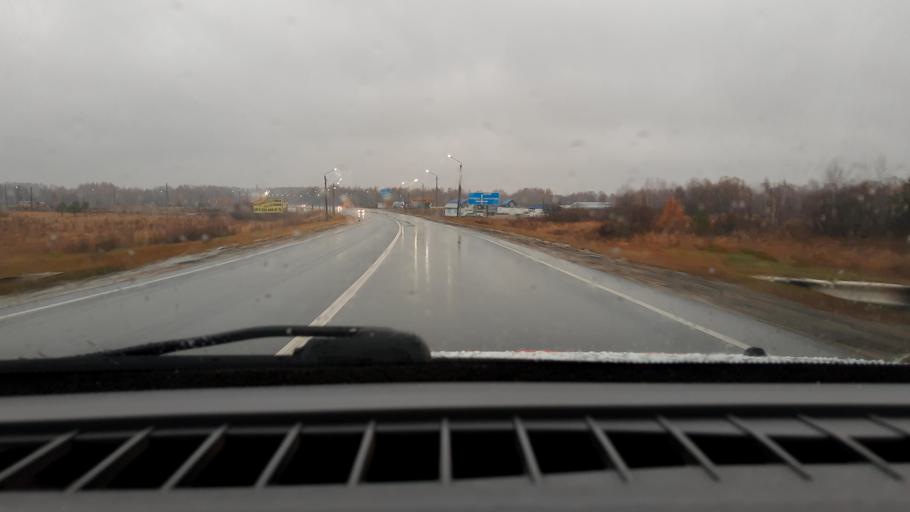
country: RU
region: Nizjnij Novgorod
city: Sitniki
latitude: 56.4977
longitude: 44.0251
